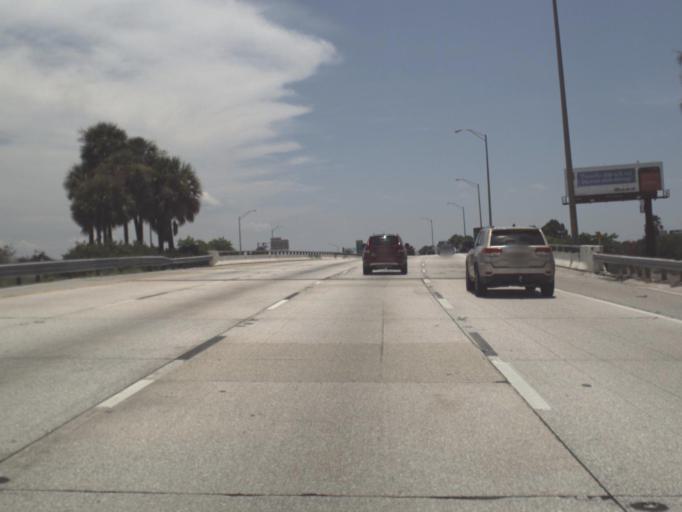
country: US
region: Florida
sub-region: Pinellas County
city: Saint Petersburg
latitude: 27.7878
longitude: -82.6609
